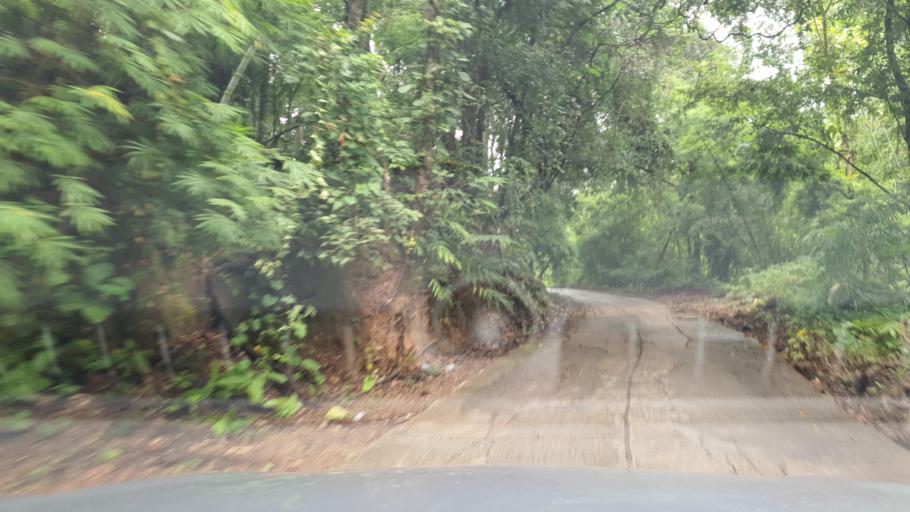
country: TH
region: Chiang Mai
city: Mae Taeng
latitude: 19.2200
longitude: 98.9255
